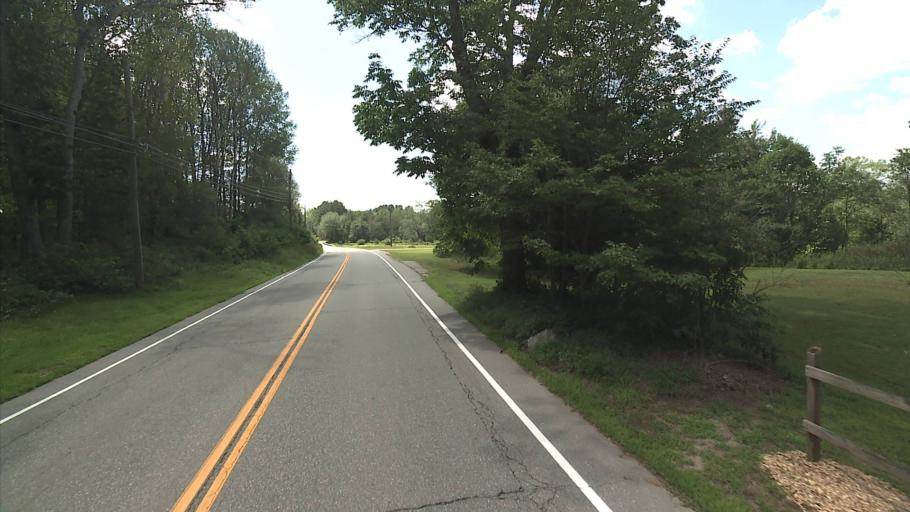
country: US
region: Connecticut
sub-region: Windham County
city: Windham
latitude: 41.8041
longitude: -72.1233
